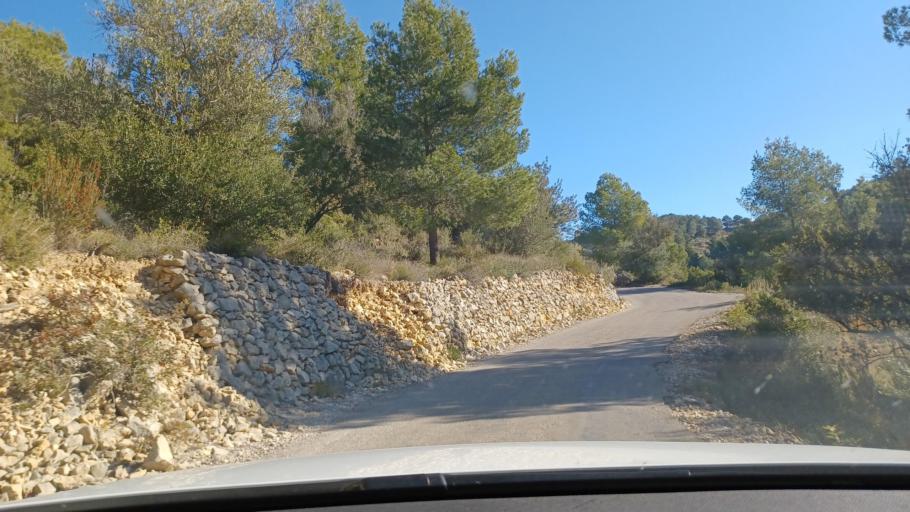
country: ES
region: Catalonia
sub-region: Provincia de Tarragona
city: Tortosa
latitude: 40.8164
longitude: 0.5638
